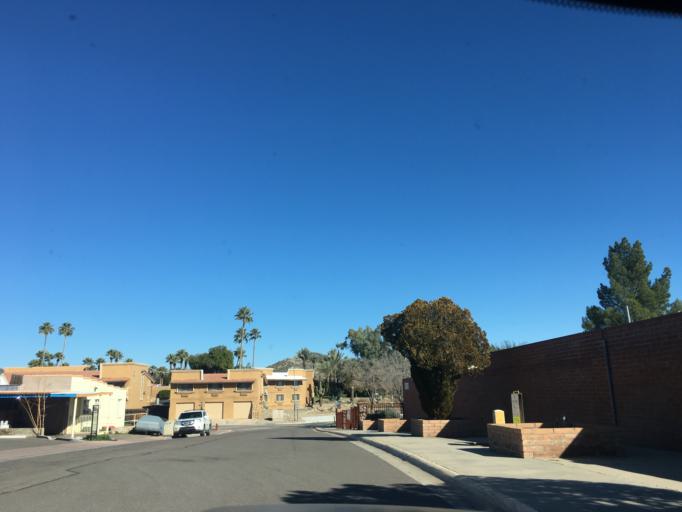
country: US
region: Arizona
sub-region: Maricopa County
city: Wickenburg
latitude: 33.9682
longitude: -112.7289
